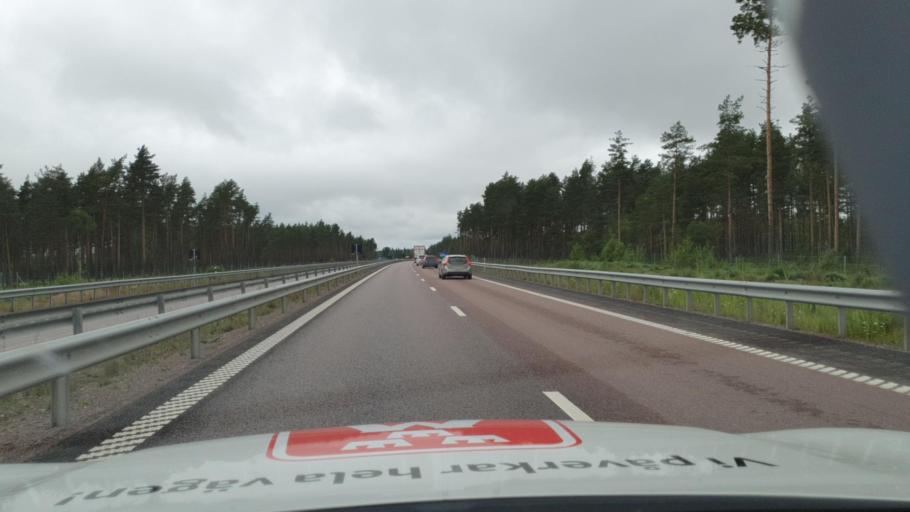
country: SE
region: Vaermland
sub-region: Kils Kommun
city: Kil
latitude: 59.3884
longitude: 13.3010
